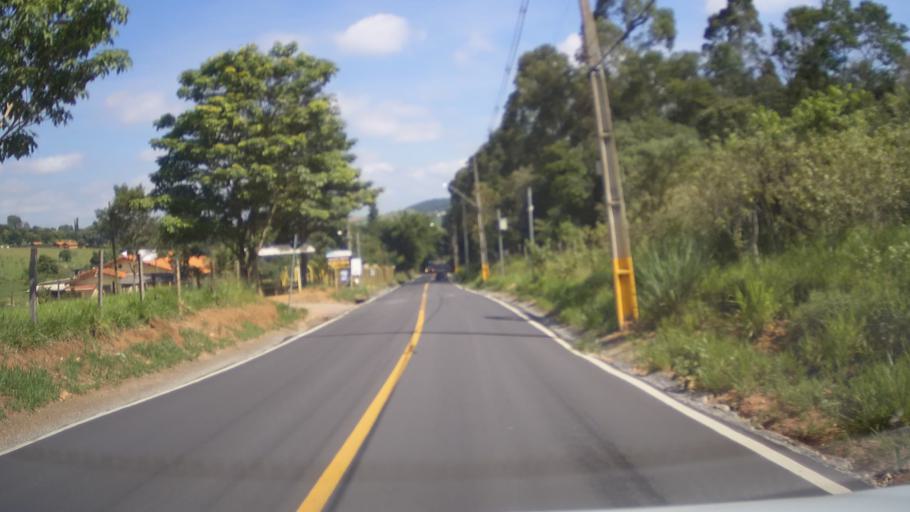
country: BR
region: Sao Paulo
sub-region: Itupeva
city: Itupeva
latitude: -23.2047
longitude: -47.0665
